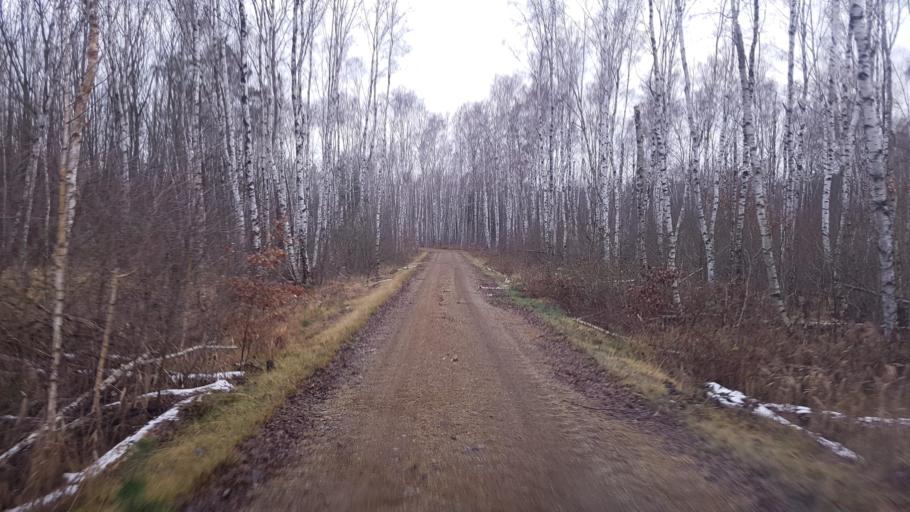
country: DE
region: Brandenburg
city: Plessa
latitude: 51.5213
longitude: 13.6829
